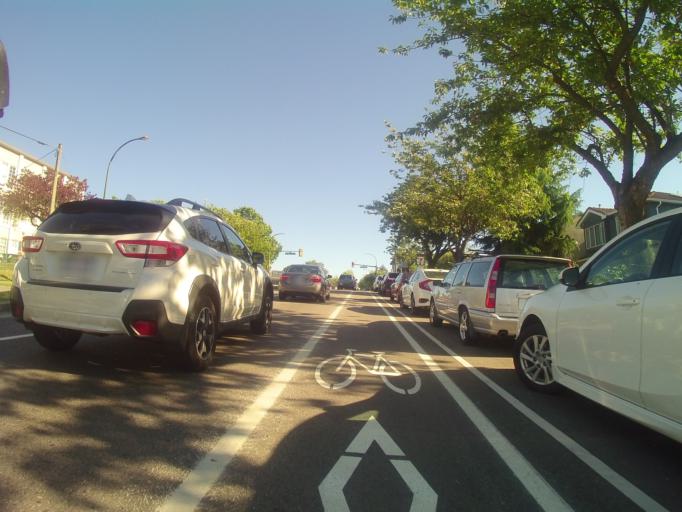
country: CA
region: British Columbia
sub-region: Fraser Valley Regional District
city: North Vancouver
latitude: 49.2514
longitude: -123.0339
